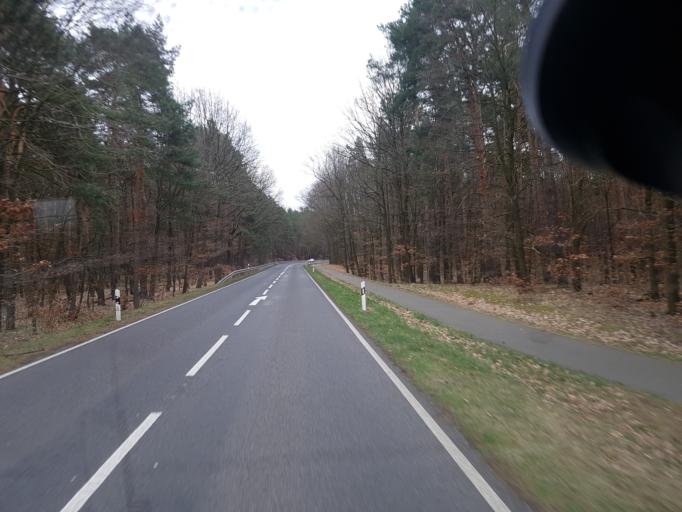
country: DE
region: Brandenburg
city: Mixdorf
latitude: 52.1869
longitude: 14.4708
